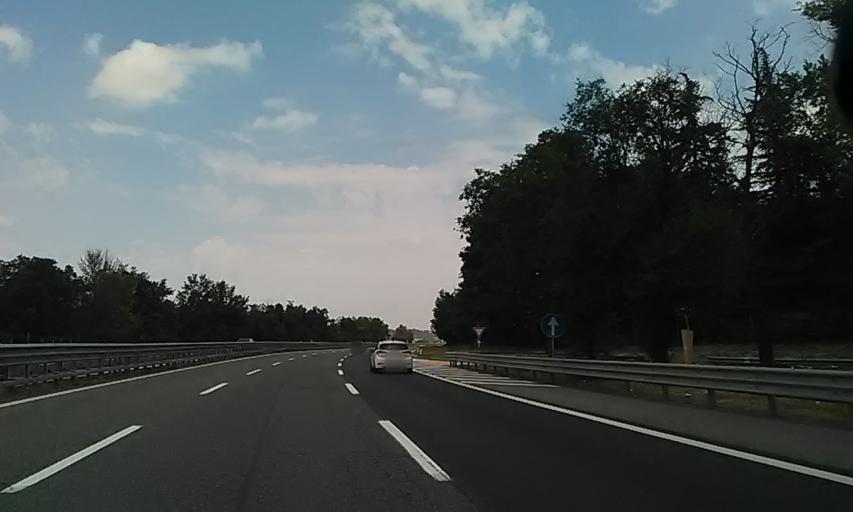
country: IT
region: Piedmont
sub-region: Provincia di Alessandria
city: Tagliolo Monferrato
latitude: 44.6418
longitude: 8.6606
